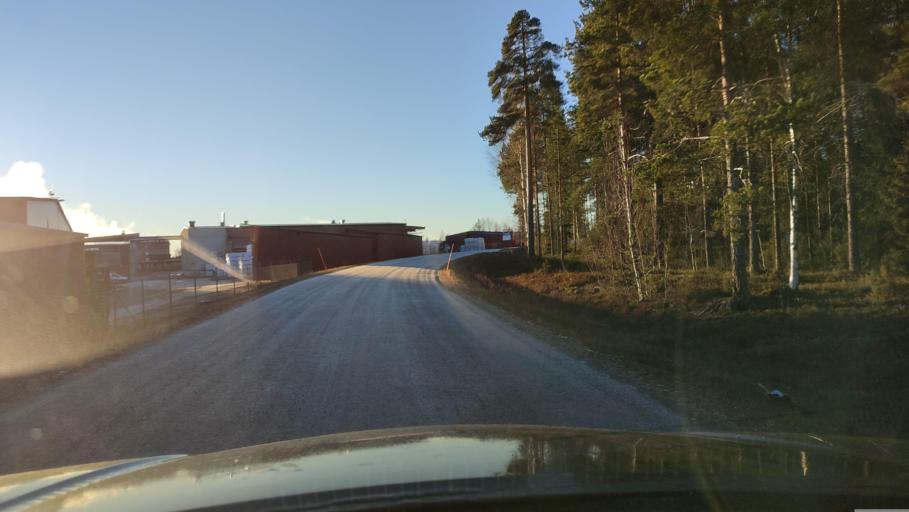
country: SE
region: Vaesterbotten
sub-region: Skelleftea Kommun
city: Viken
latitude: 64.7043
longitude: 20.9049
